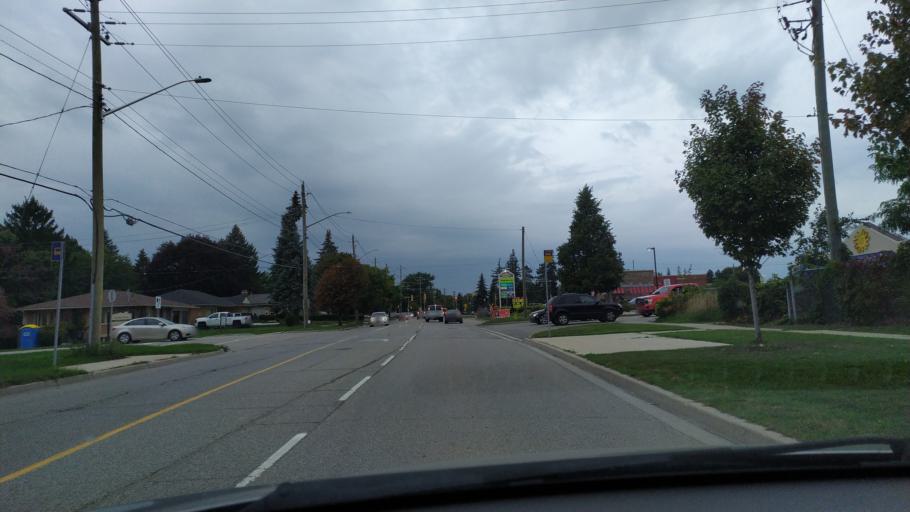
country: CA
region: Ontario
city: Waterloo
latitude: 43.4879
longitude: -80.4920
